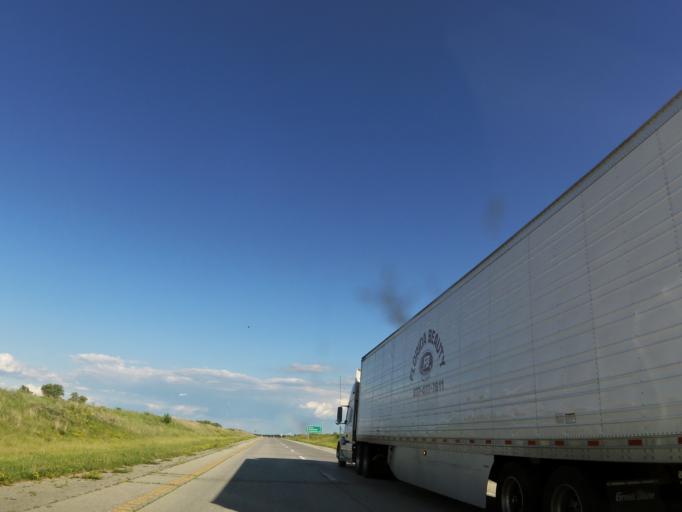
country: US
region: Missouri
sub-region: Pike County
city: Bowling Green
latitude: 39.2721
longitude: -91.0874
